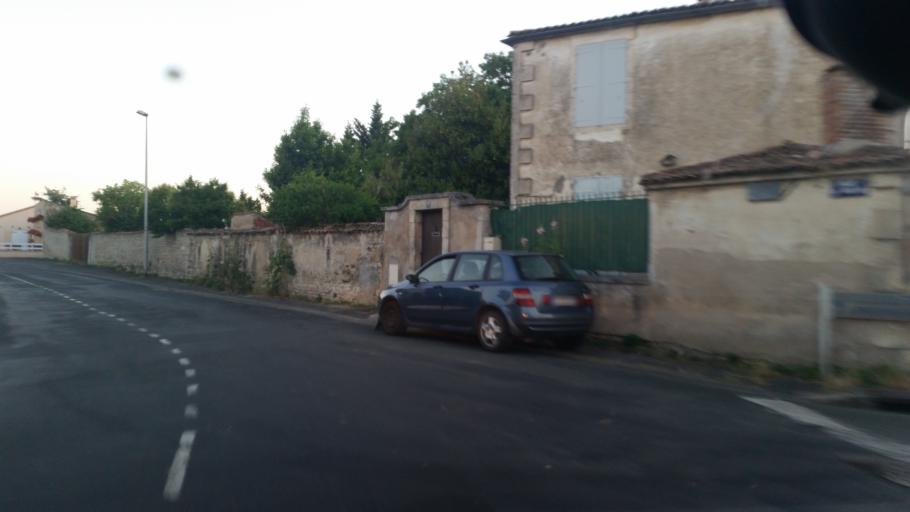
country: FR
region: Poitou-Charentes
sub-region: Departement de la Charente-Maritime
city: Marans
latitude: 46.3081
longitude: -1.0001
